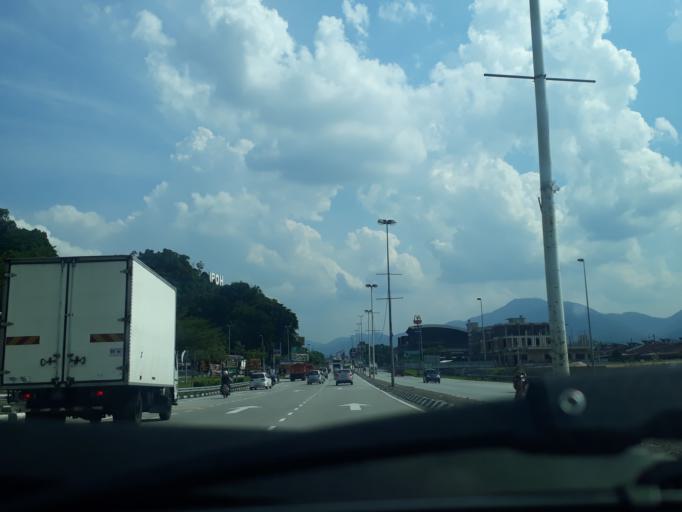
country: MY
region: Perak
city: Ipoh
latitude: 4.6355
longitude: 101.0901
